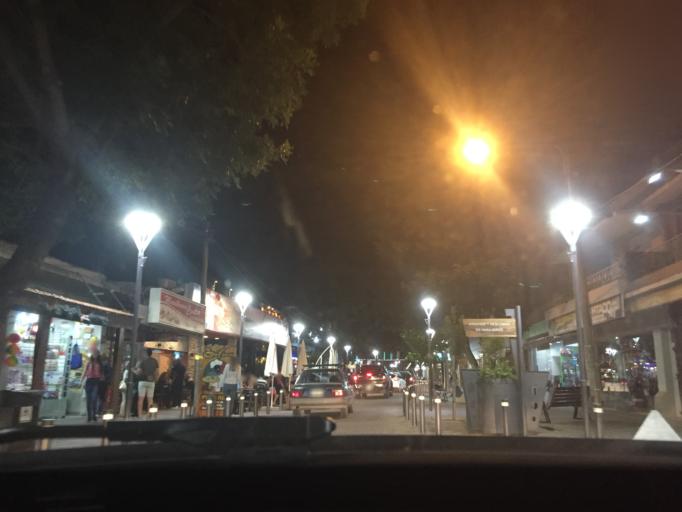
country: AR
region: Cordoba
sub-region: Departamento de Calamuchita
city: Santa Rosa de Calamuchita
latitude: -32.0698
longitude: -64.5366
